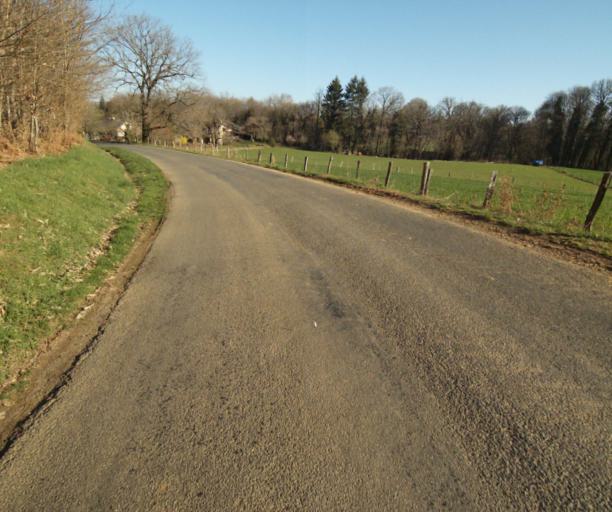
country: FR
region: Limousin
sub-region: Departement de la Correze
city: Saint-Clement
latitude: 45.3780
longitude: 1.6452
